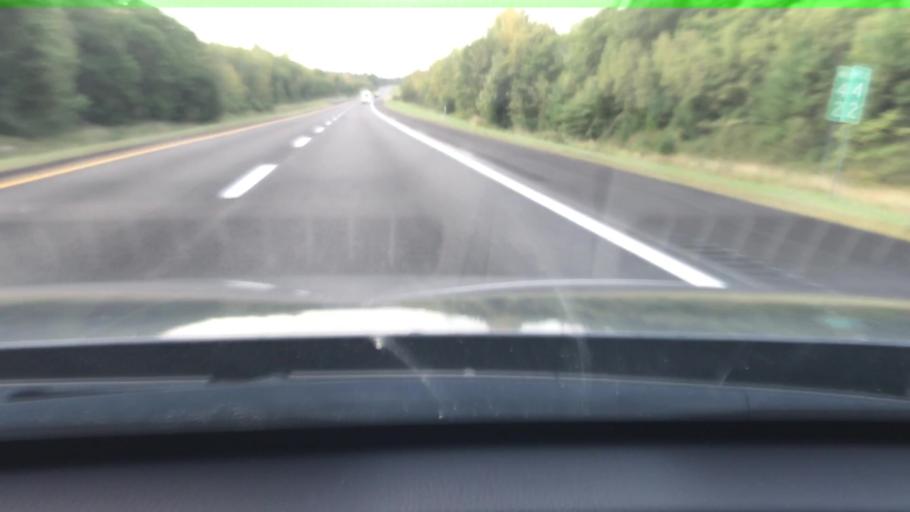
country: US
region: Maine
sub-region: Sagadahoc County
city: Richmond
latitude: 44.0800
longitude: -69.8781
